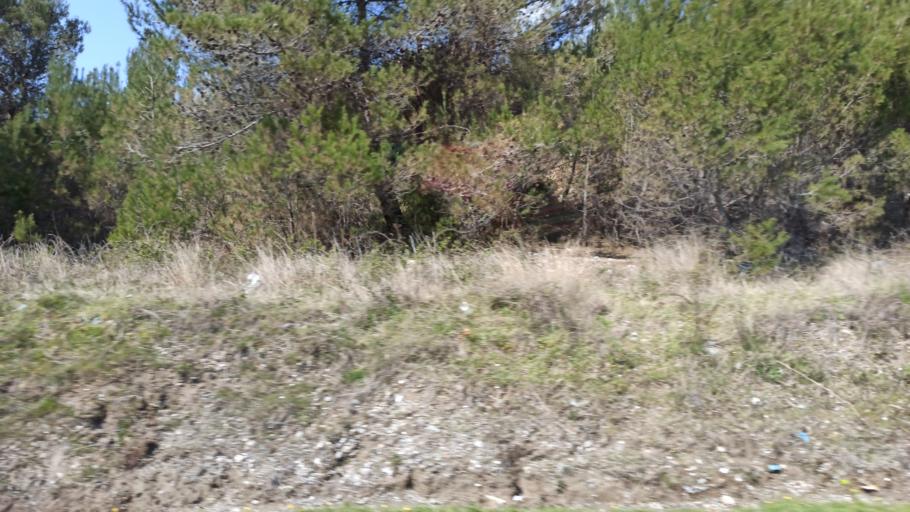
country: AL
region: Shkoder
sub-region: Rrethi i Shkodres
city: Guri i Zi
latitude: 42.0616
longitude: 19.5499
